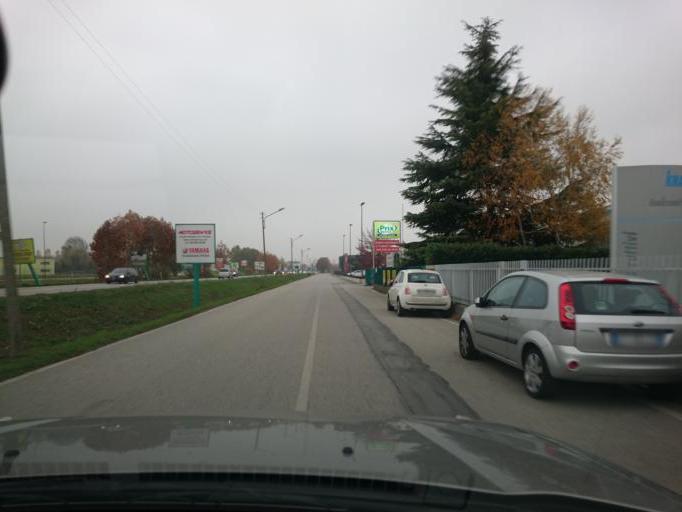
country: IT
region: Veneto
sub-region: Provincia di Padova
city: Legnaro
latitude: 45.3514
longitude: 11.9556
